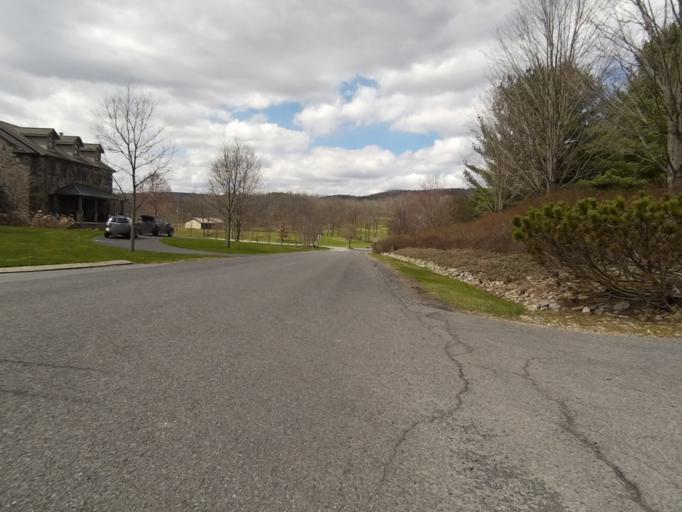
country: US
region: Pennsylvania
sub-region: Centre County
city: Park Forest Village
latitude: 40.8277
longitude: -77.9345
